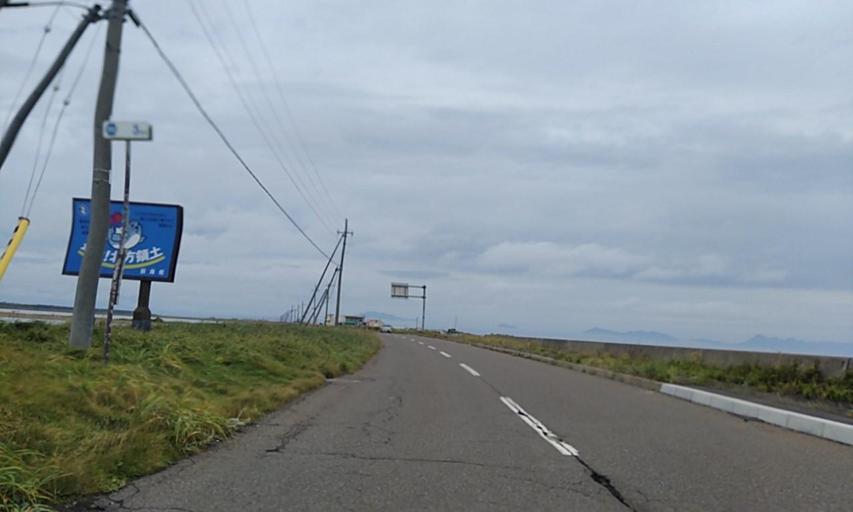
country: JP
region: Hokkaido
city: Shibetsu
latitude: 43.5914
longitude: 145.3339
